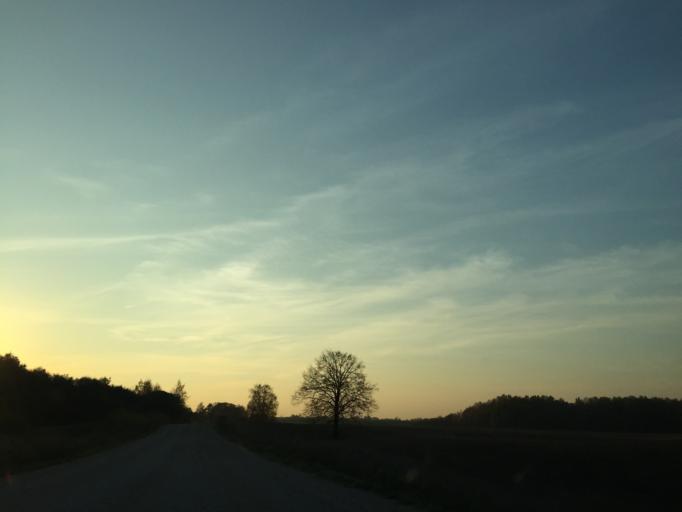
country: LV
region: Priekule
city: Priekule
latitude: 56.4729
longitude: 21.6148
